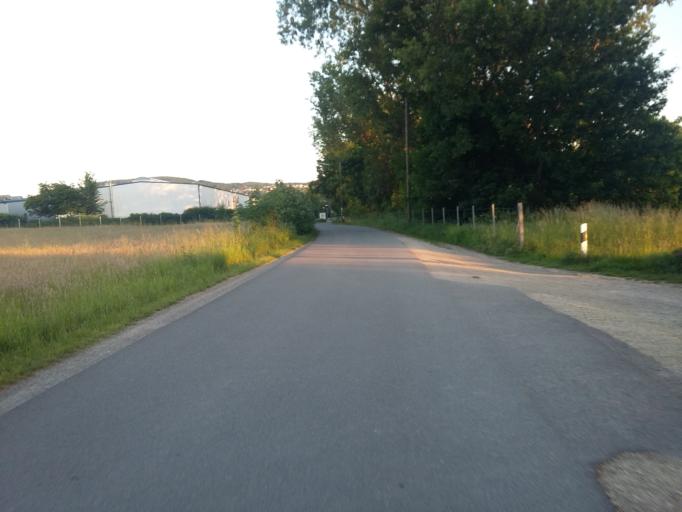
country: DE
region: North Rhine-Westphalia
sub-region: Regierungsbezirk Detmold
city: Vlotho
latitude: 52.1837
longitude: 8.8661
